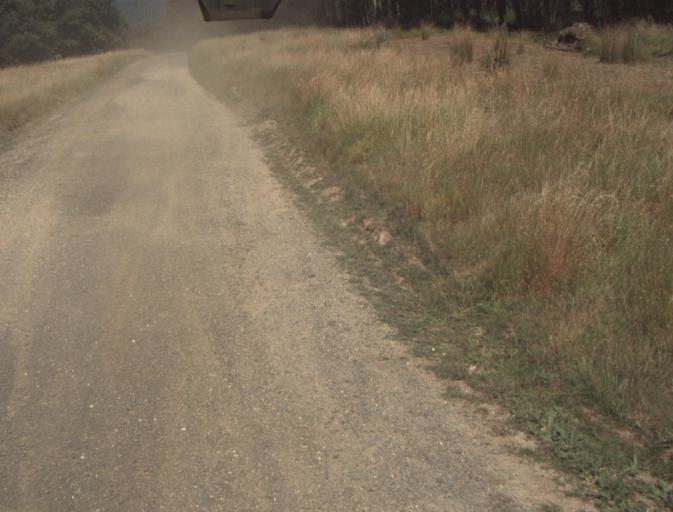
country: AU
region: Tasmania
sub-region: Dorset
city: Scottsdale
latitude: -41.2715
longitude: 147.3503
